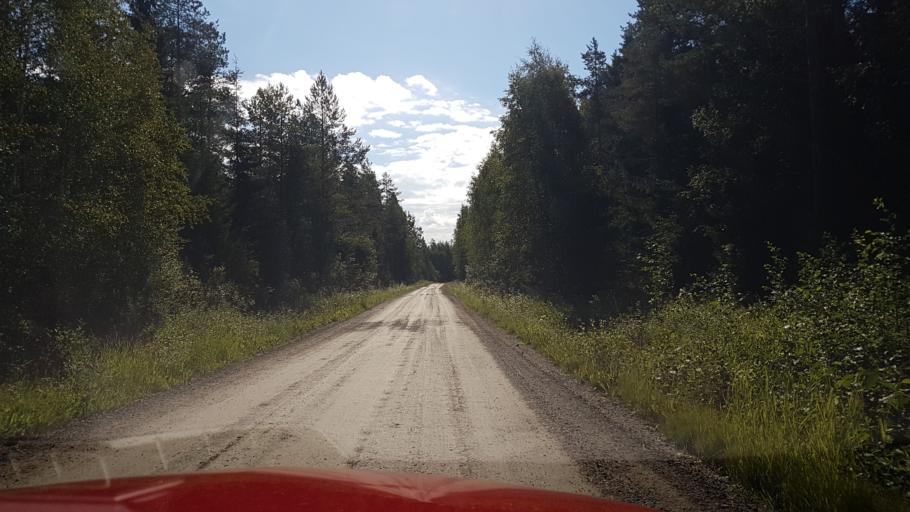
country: FI
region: Northern Ostrobothnia
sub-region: Ylivieska
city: Himanka
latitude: 64.0808
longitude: 23.7979
